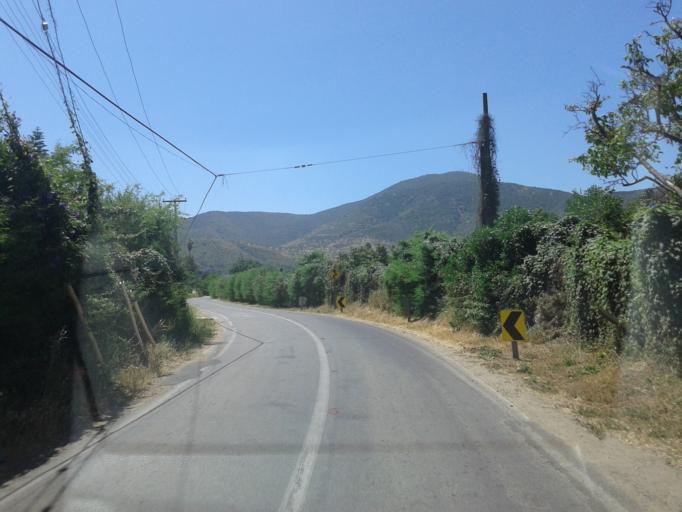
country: CL
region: Valparaiso
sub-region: Provincia de Quillota
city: Hacienda La Calera
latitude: -32.8438
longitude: -71.1911
